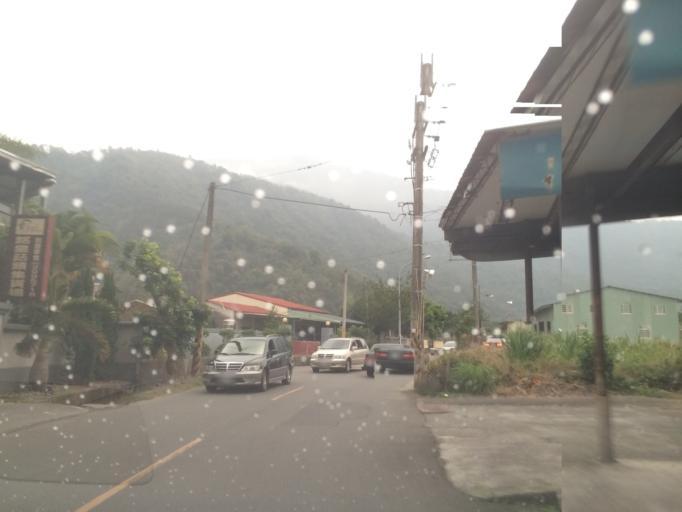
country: TW
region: Taiwan
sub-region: Nantou
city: Puli
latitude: 23.9501
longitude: 120.9850
